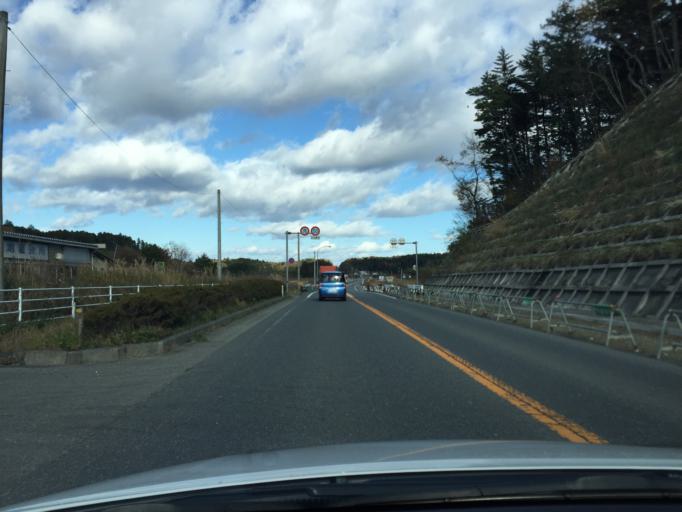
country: JP
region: Fukushima
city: Namie
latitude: 37.4619
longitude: 141.0100
